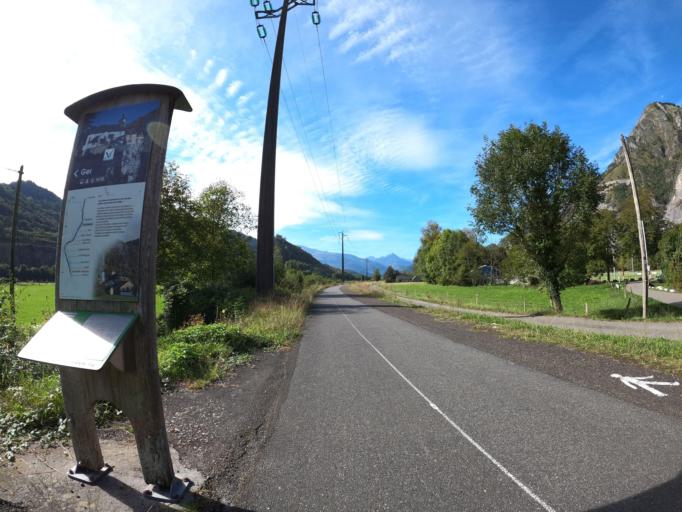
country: FR
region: Midi-Pyrenees
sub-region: Departement des Hautes-Pyrenees
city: Lourdes
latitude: 43.0522
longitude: -0.0459
